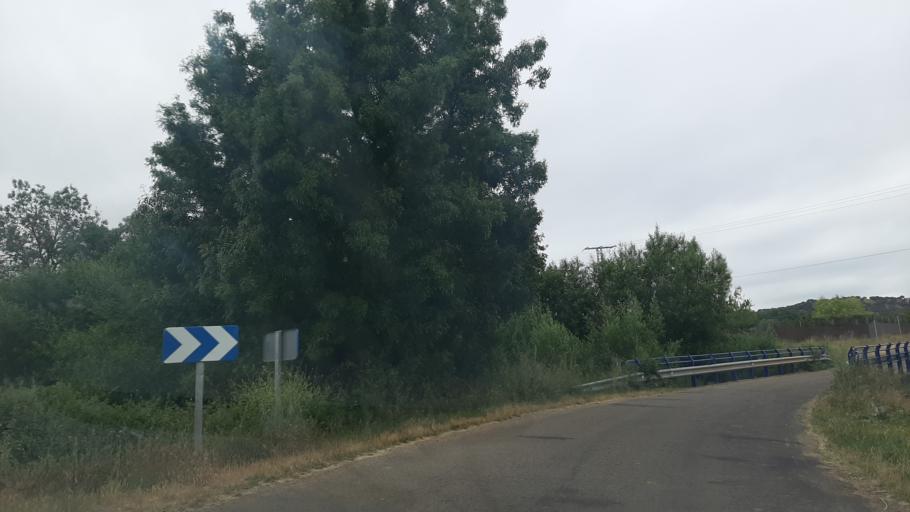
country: ES
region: Castille and Leon
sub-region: Provincia de Salamanca
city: Pastores
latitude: 40.5643
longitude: -6.4854
